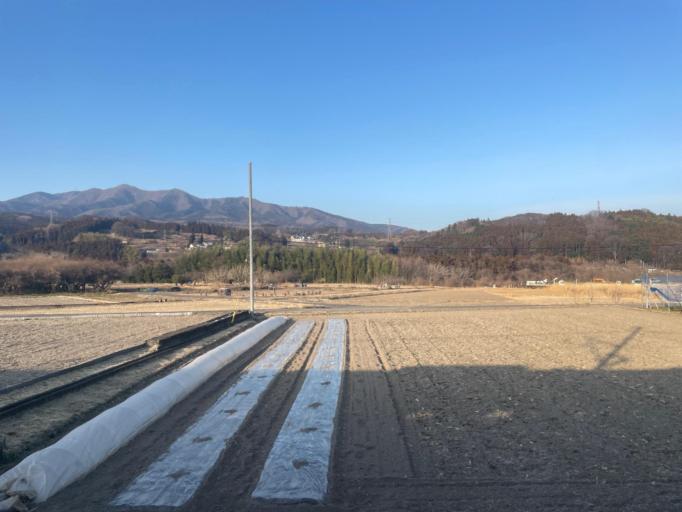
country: JP
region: Gunma
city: Shibukawa
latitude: 36.5321
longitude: 138.9729
